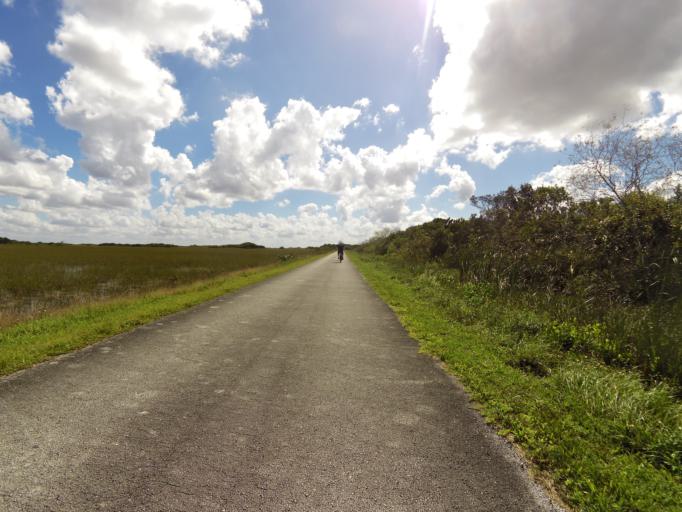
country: US
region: Florida
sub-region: Miami-Dade County
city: The Hammocks
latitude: 25.7310
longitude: -80.7667
